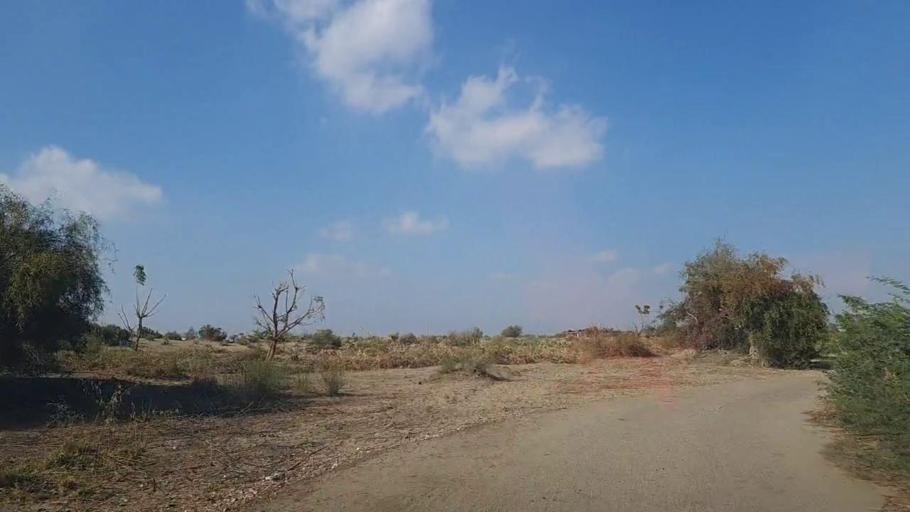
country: PK
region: Sindh
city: Tando Mittha Khan
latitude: 26.0120
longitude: 69.2477
